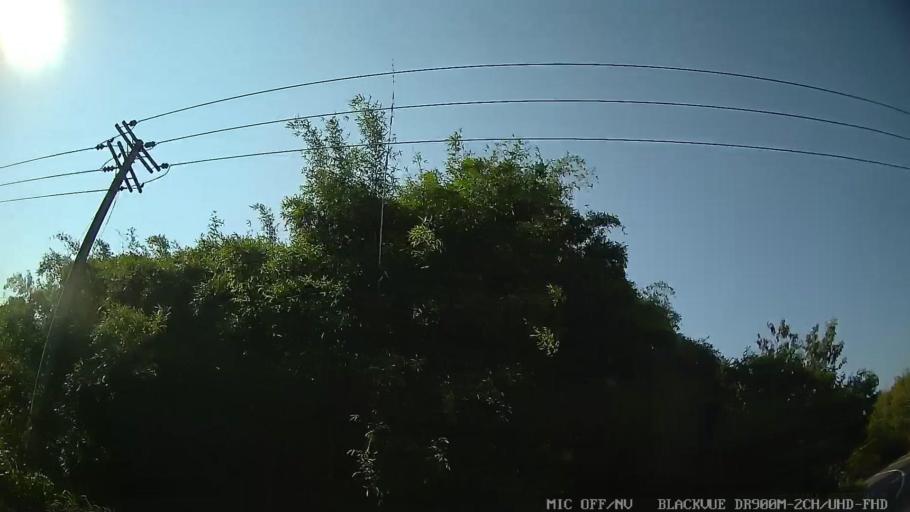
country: BR
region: Sao Paulo
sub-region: Itatiba
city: Itatiba
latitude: -22.9832
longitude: -46.8366
